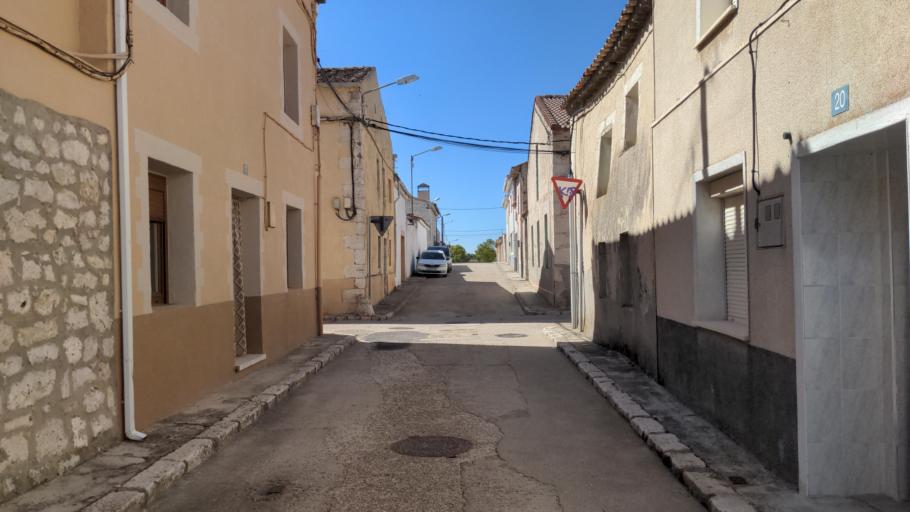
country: ES
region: Castille and Leon
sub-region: Provincia de Valladolid
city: Tudela de Duero
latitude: 41.5369
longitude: -4.5333
